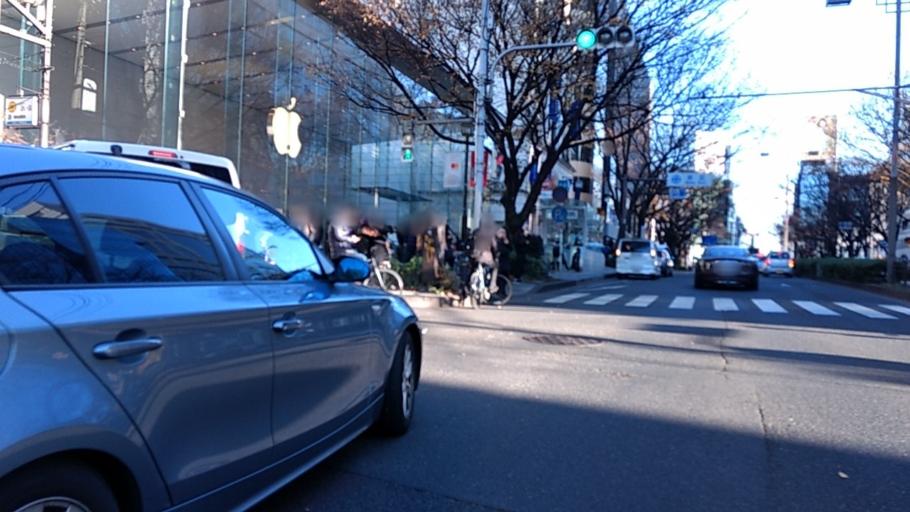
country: JP
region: Tokyo
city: Tokyo
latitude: 35.6661
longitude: 139.7106
